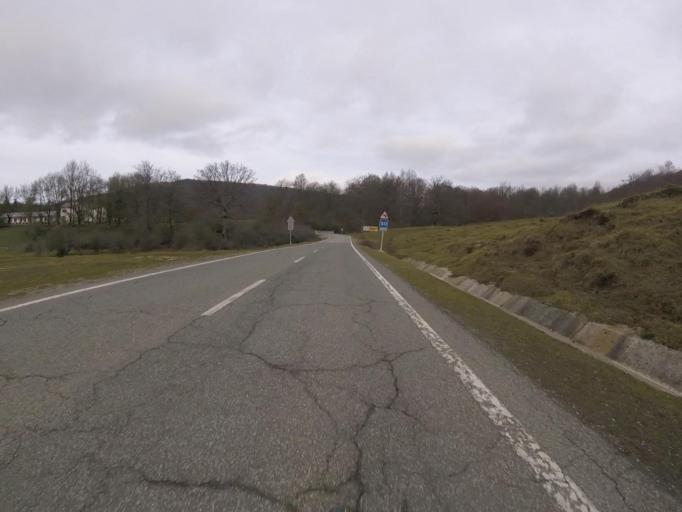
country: ES
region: Navarre
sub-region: Provincia de Navarra
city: Olazagutia
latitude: 42.8501
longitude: -2.1712
